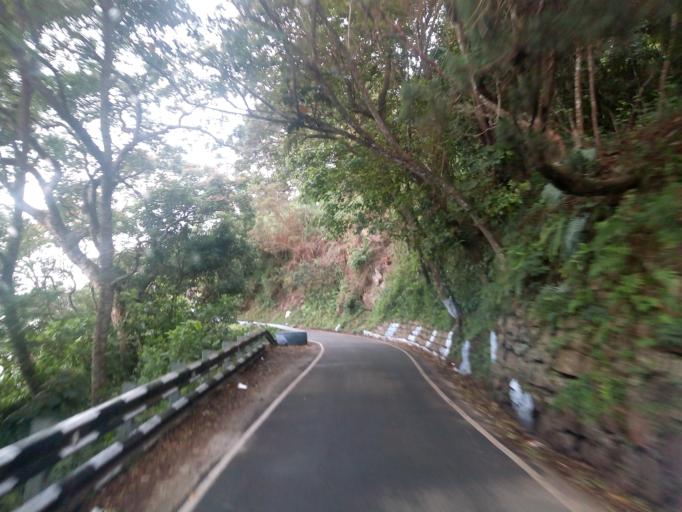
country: IN
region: Tamil Nadu
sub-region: Nilgiri
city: Kotagiri
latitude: 11.3615
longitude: 76.8467
